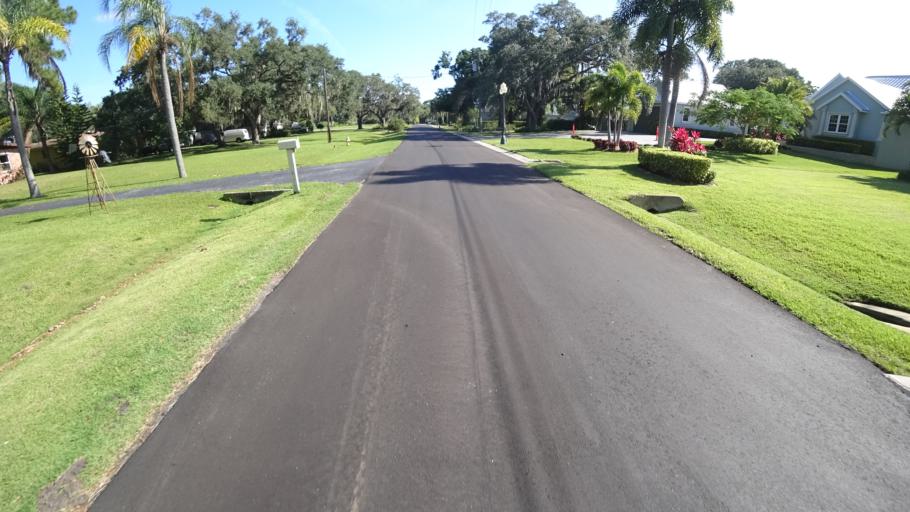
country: US
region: Florida
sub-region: Manatee County
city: Ellenton
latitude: 27.5210
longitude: -82.5148
